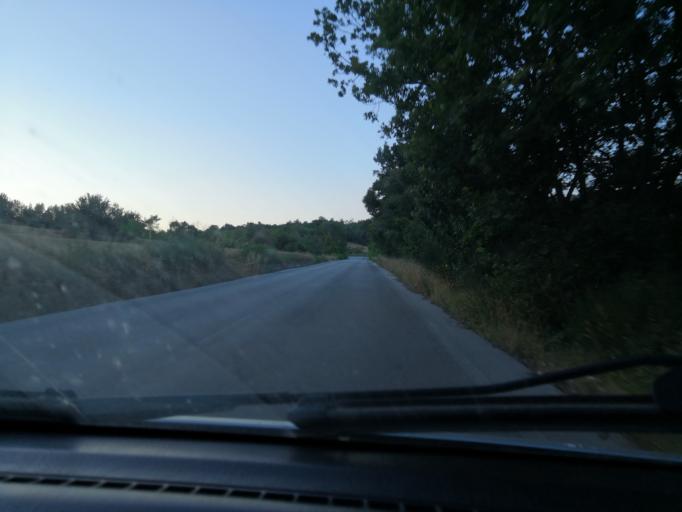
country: IT
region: Molise
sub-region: Provincia di Campobasso
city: Jelsi
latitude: 41.5120
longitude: 14.7747
